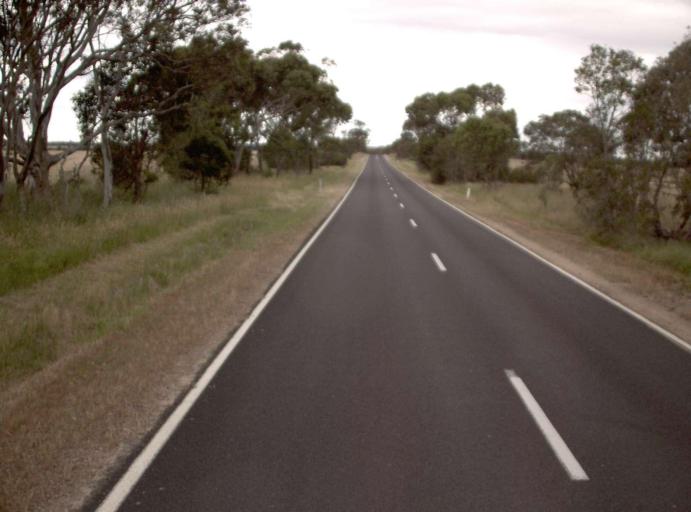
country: AU
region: Victoria
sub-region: Wellington
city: Sale
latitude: -37.9968
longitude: 147.2101
